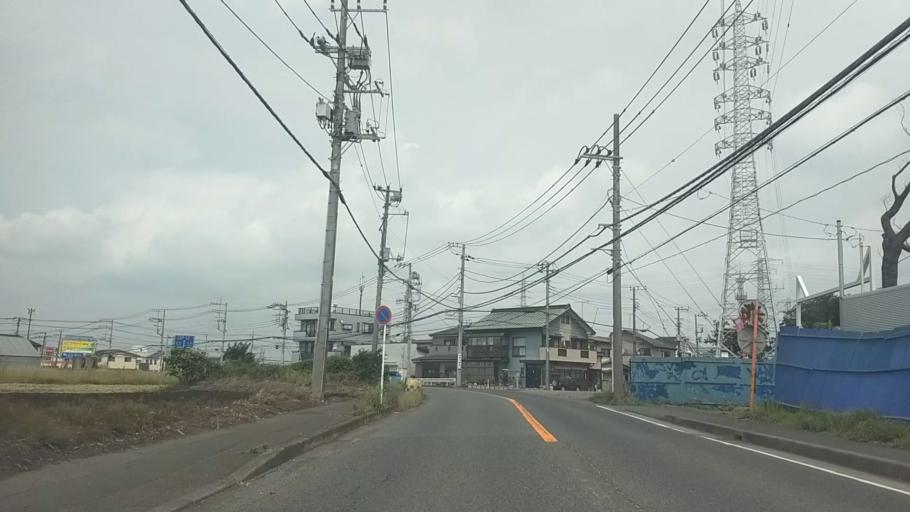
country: JP
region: Kanagawa
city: Fujisawa
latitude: 35.3799
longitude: 139.4851
